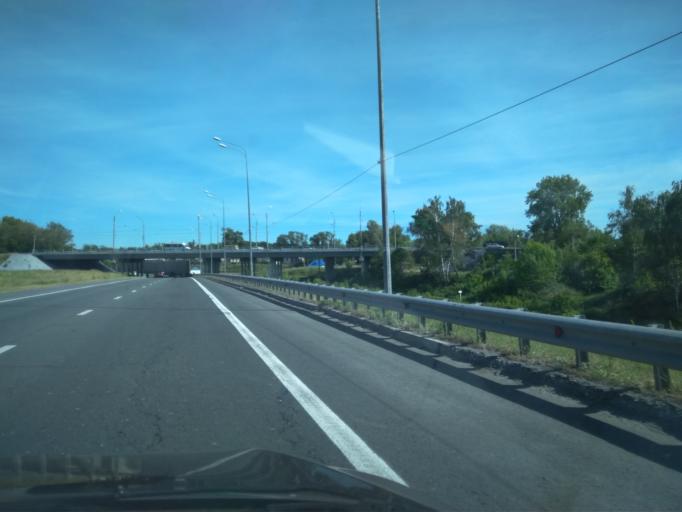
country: RU
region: Ulyanovsk
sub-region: Ulyanovskiy Rayon
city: Ulyanovsk
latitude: 54.3361
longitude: 48.5237
